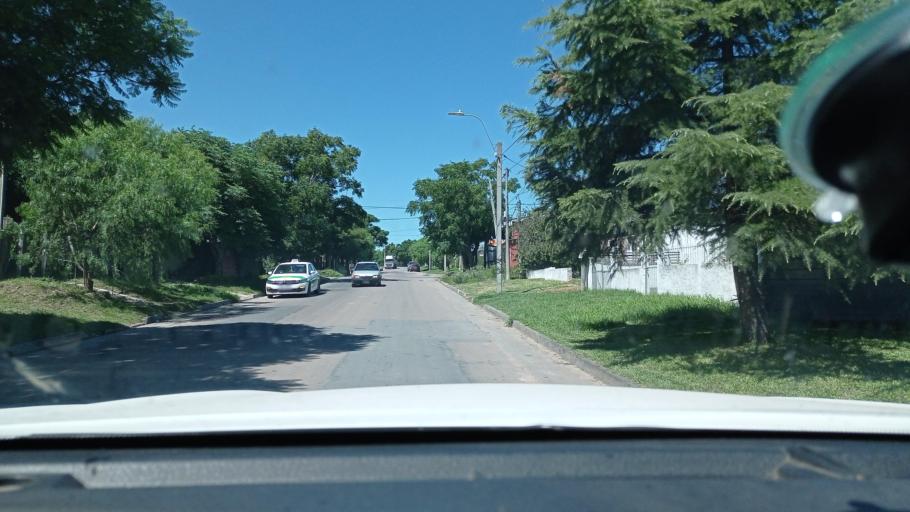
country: UY
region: Canelones
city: Las Piedras
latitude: -34.7365
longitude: -56.2185
